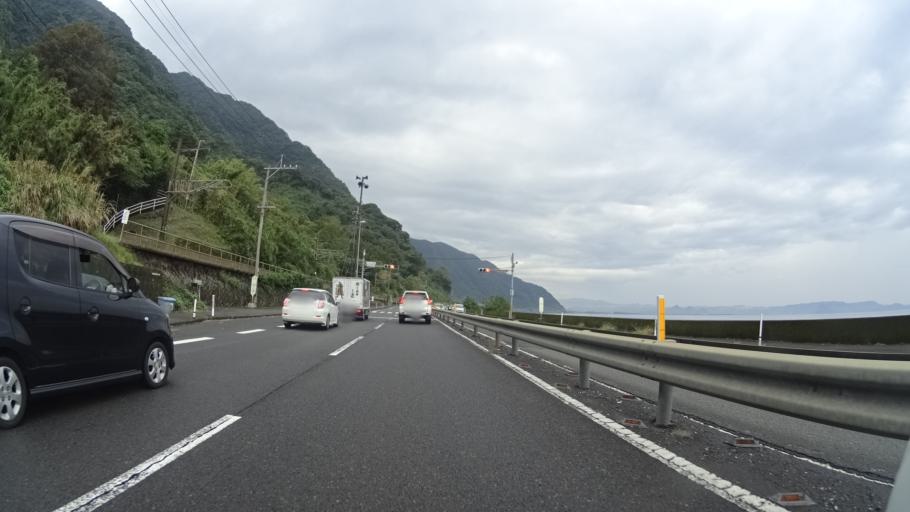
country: JP
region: Kagoshima
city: Kajiki
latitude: 31.6673
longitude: 130.6126
